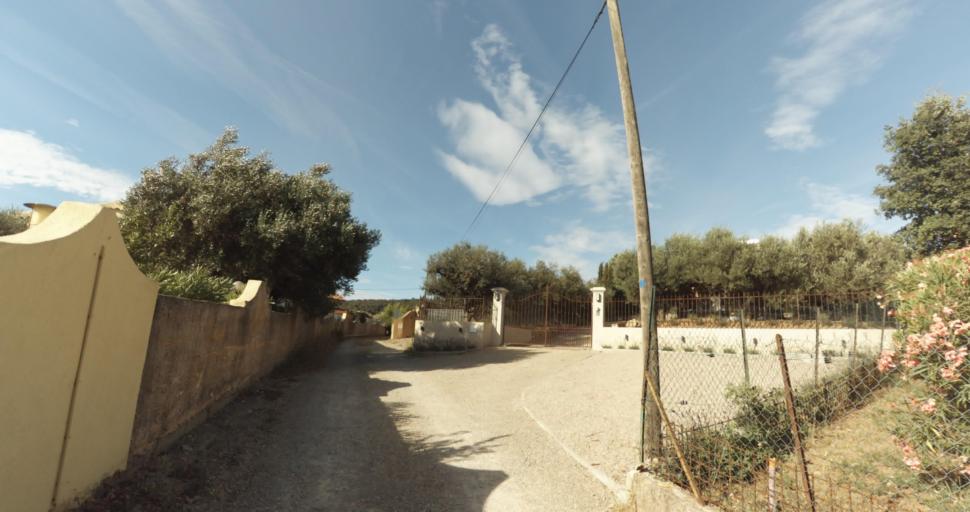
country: FR
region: Provence-Alpes-Cote d'Azur
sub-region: Departement du Var
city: Gassin
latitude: 43.2309
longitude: 6.5761
